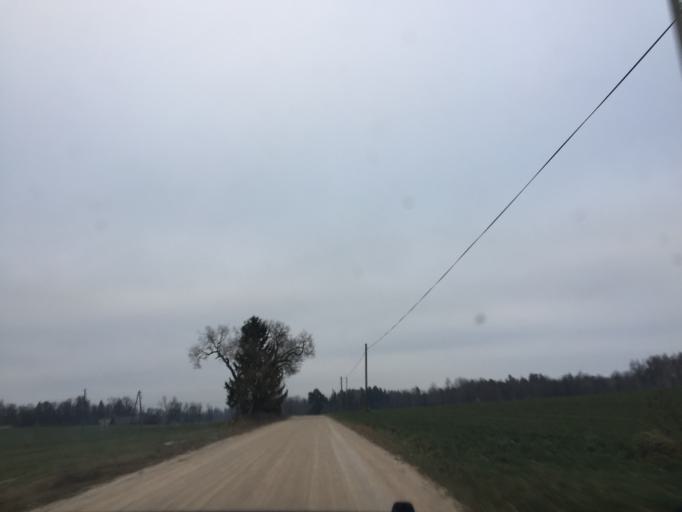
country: LV
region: Raunas
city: Rauna
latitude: 57.3175
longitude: 25.5954
